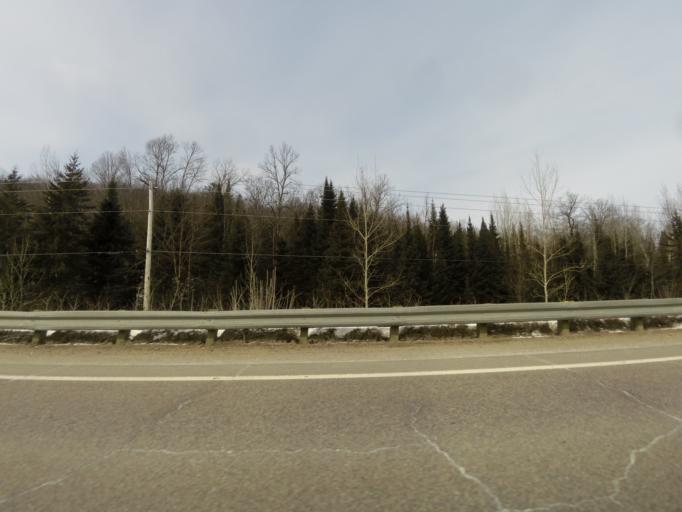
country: CA
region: Quebec
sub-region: Laurentides
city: Mont-Laurier
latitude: 46.3254
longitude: -75.5448
